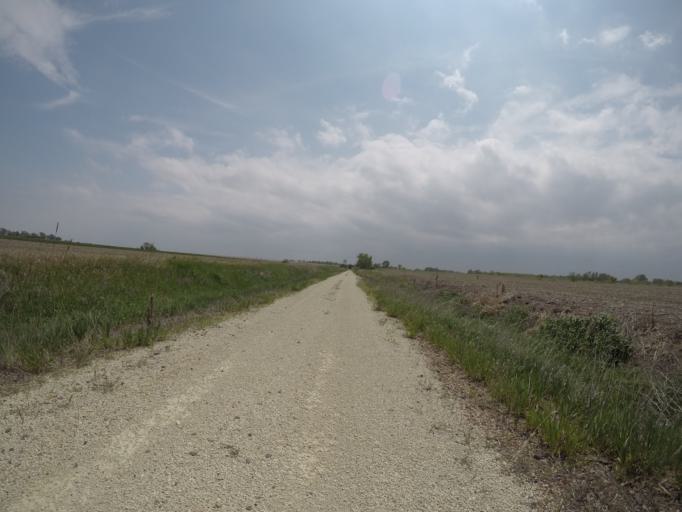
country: US
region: Nebraska
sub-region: Gage County
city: Wymore
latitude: 40.2137
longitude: -96.6627
